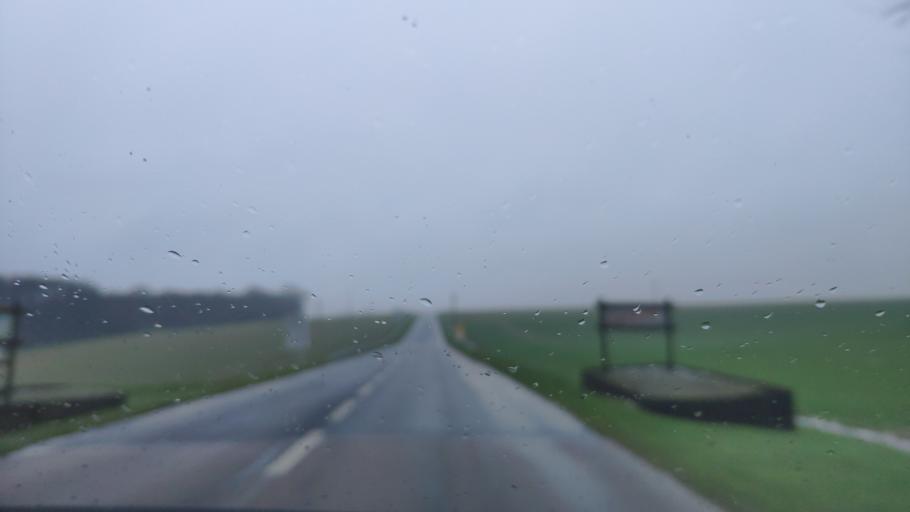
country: FR
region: Haute-Normandie
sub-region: Departement de la Seine-Maritime
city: Doudeville
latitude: 49.7263
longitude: 0.7804
